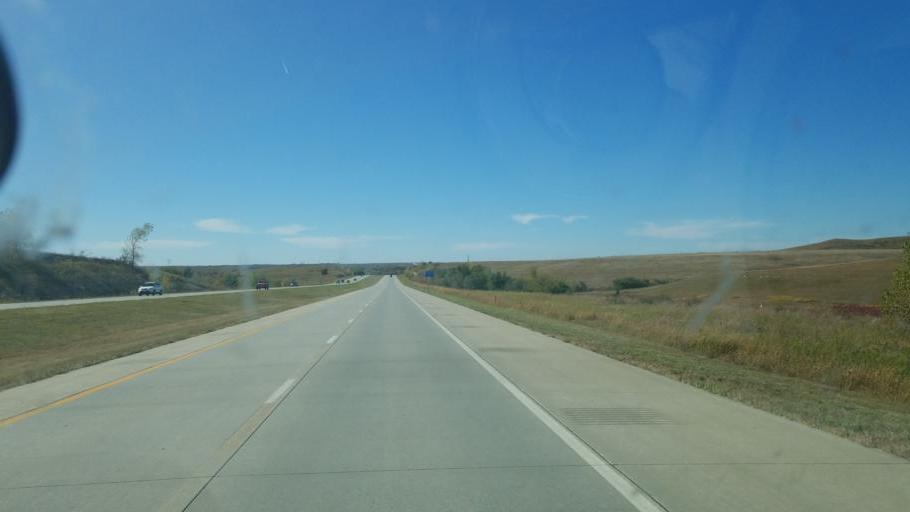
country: US
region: Kansas
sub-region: Riley County
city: Ogden
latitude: 39.0661
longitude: -96.5982
